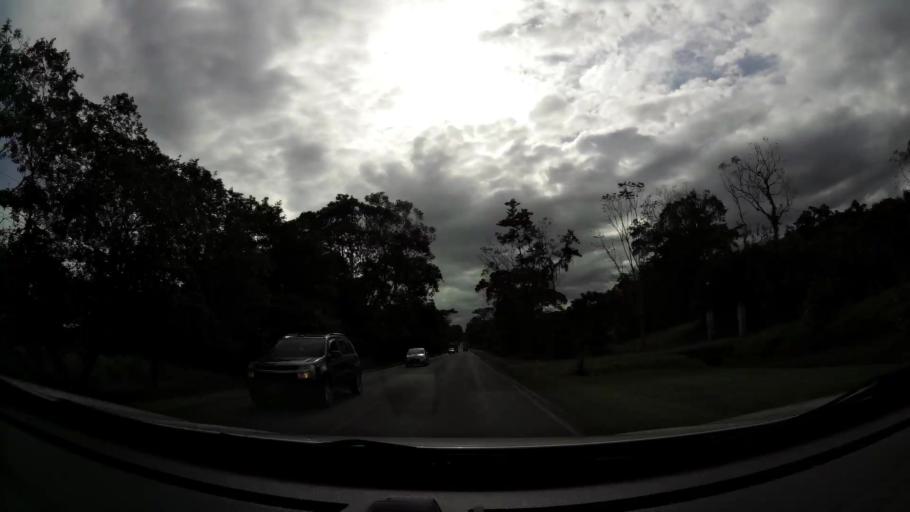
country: CR
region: Limon
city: Pocora
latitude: 10.1873
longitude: -83.6333
